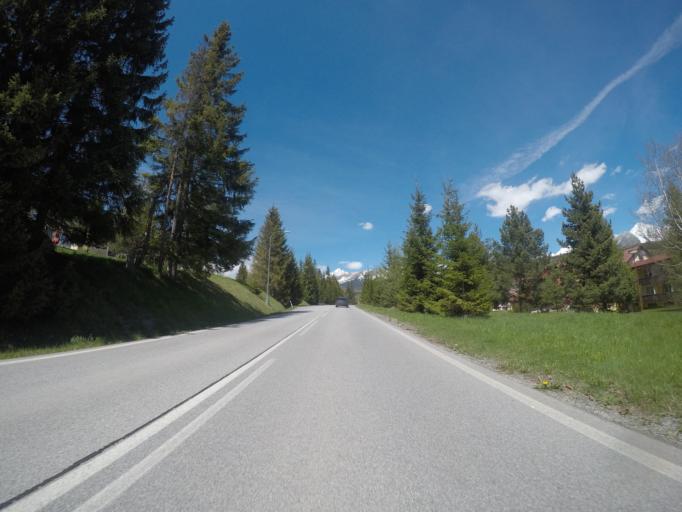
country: SK
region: Presovsky
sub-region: Okres Poprad
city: Strba
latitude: 49.0909
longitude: 20.0712
